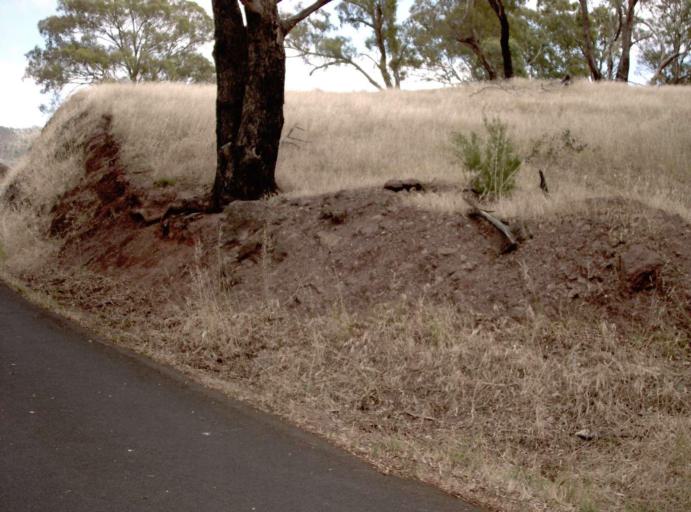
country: AU
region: Victoria
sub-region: Wellington
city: Heyfield
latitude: -37.6572
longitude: 146.6432
